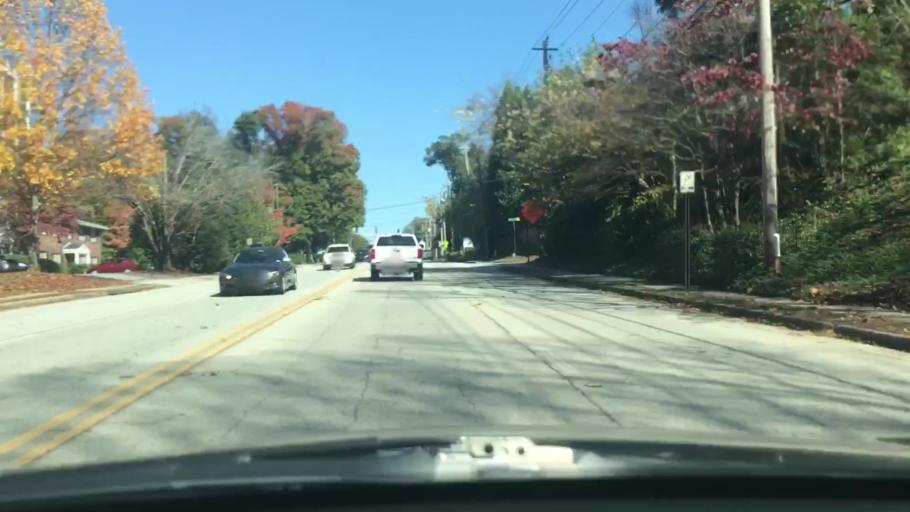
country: US
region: Georgia
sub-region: DeKalb County
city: Decatur
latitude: 33.7885
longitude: -84.2887
